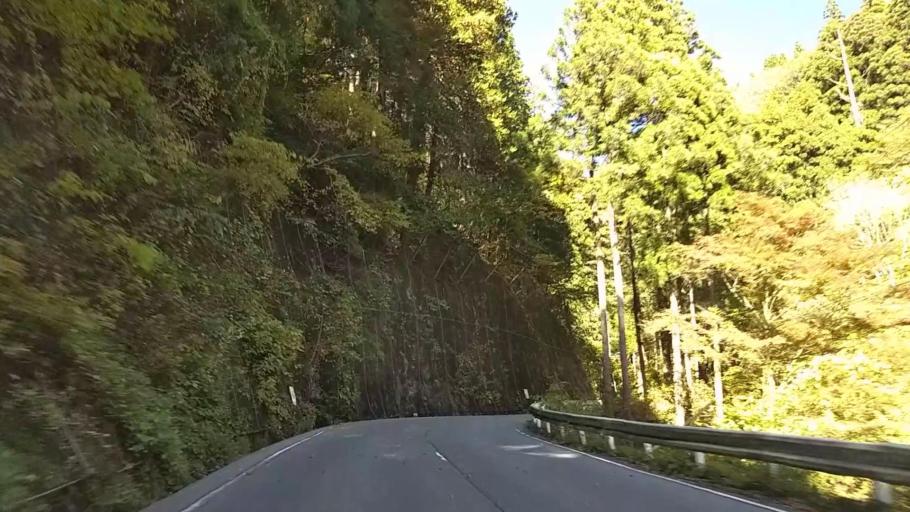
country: JP
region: Yamanashi
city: Uenohara
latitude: 35.6909
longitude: 139.0449
